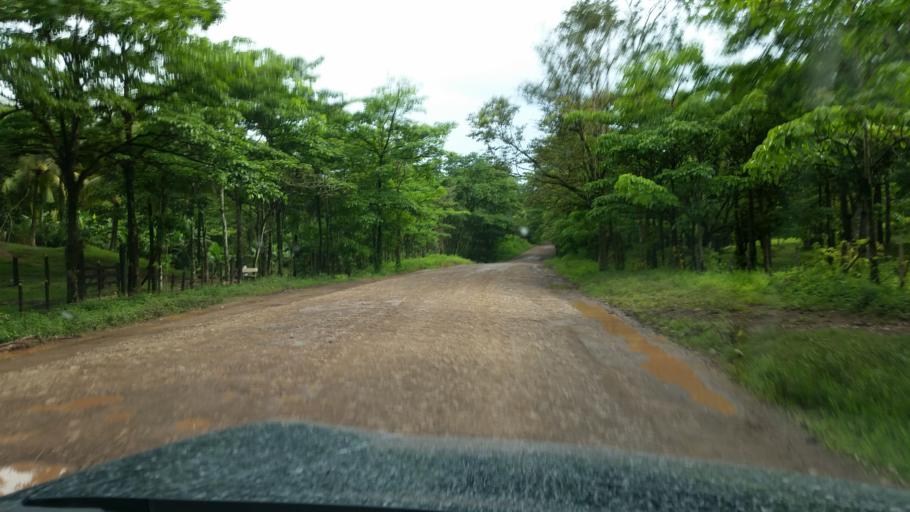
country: NI
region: Atlantico Norte (RAAN)
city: Siuna
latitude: 13.4507
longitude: -84.8543
